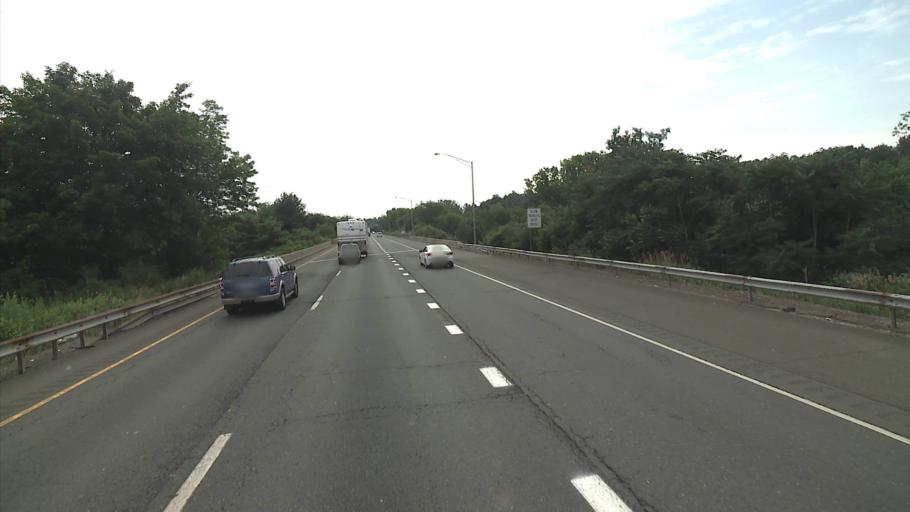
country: US
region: Connecticut
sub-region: Fairfield County
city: Newtown
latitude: 41.4151
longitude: -73.2789
